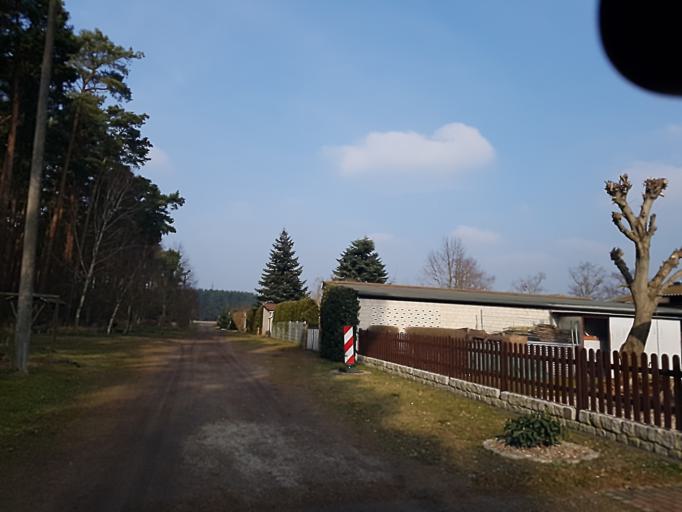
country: DE
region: Brandenburg
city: Wollin
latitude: 52.2844
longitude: 12.4660
